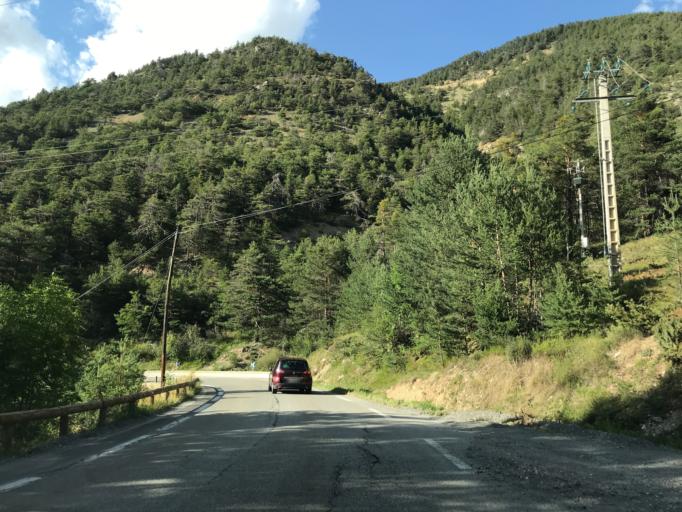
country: FR
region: Provence-Alpes-Cote d'Azur
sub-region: Departement des Hautes-Alpes
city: Briancon
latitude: 44.8835
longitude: 6.6595
